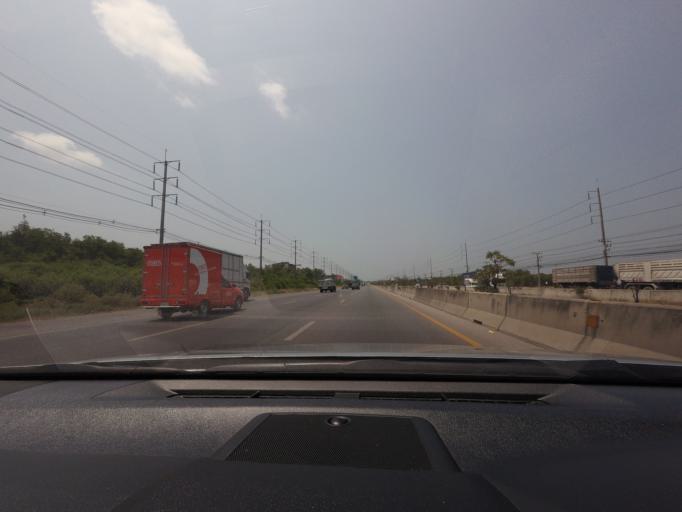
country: TH
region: Samut Sakhon
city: Ban Phaeo
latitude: 13.5170
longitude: 100.1629
